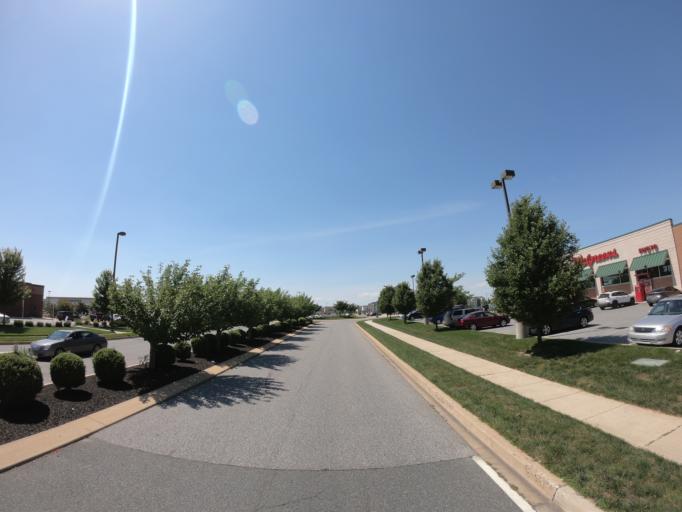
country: US
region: Delaware
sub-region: New Castle County
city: Middletown
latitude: 39.4477
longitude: -75.7315
